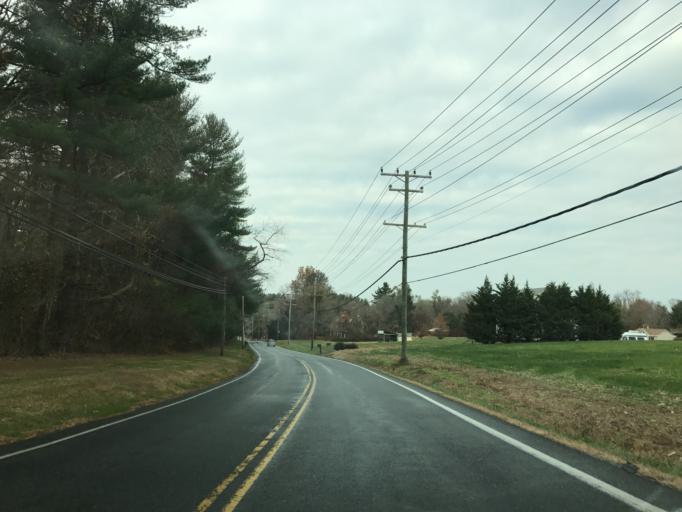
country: US
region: Maryland
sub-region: Harford County
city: Jarrettsville
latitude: 39.6047
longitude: -76.4421
